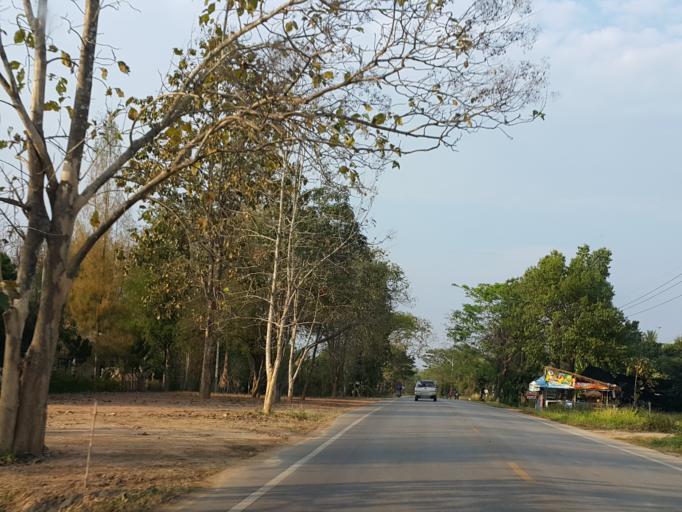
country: TH
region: Lampang
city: Chae Hom
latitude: 18.5150
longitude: 99.4759
